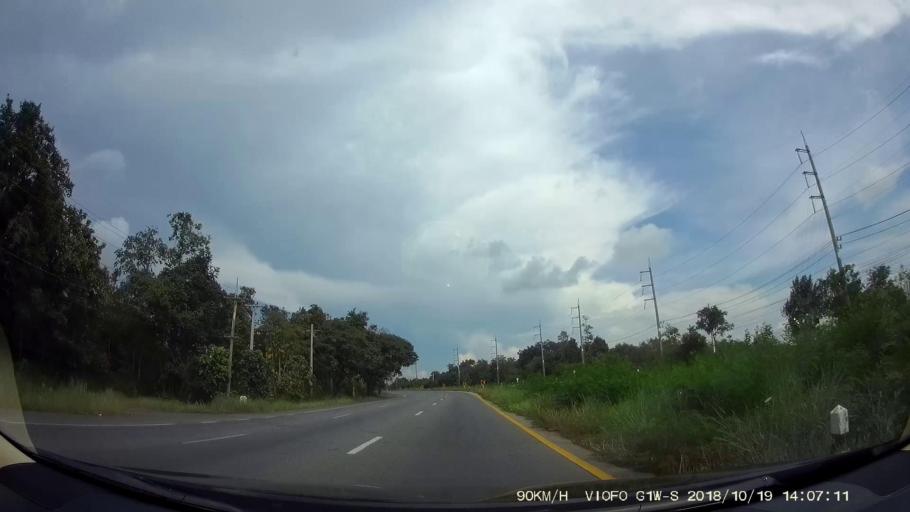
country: TH
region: Chaiyaphum
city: Chaiyaphum
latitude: 15.8917
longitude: 102.1140
